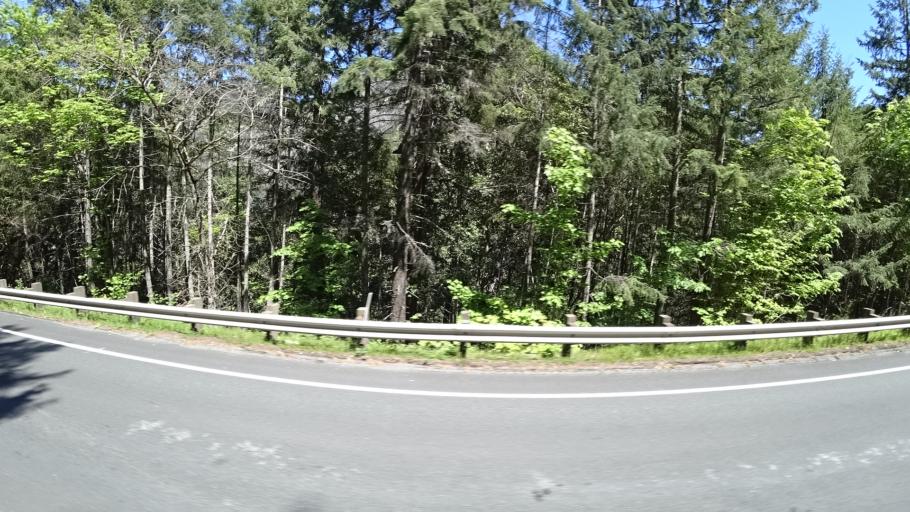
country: US
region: California
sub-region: Humboldt County
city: Willow Creek
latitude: 40.8499
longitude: -123.4878
